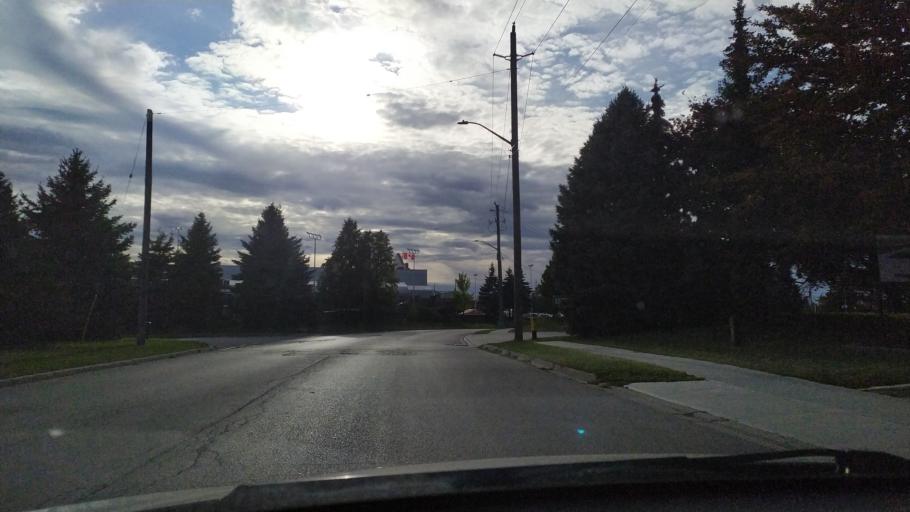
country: CA
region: Ontario
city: Waterloo
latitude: 43.5038
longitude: -80.5317
